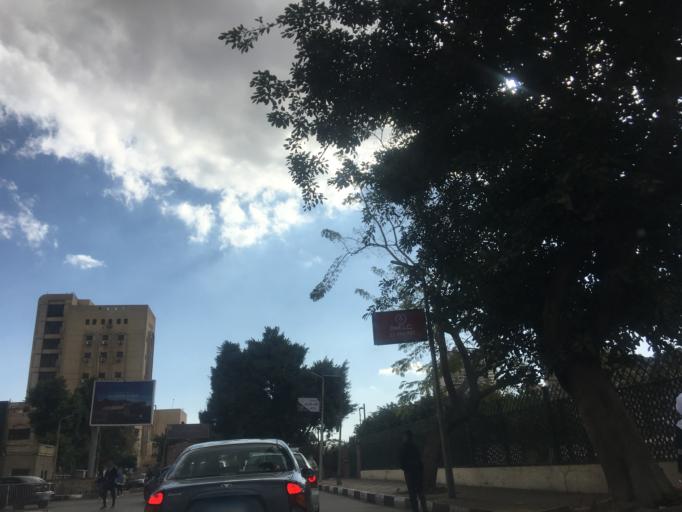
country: EG
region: Muhafazat al Qahirah
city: Cairo
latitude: 30.0445
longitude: 31.2206
